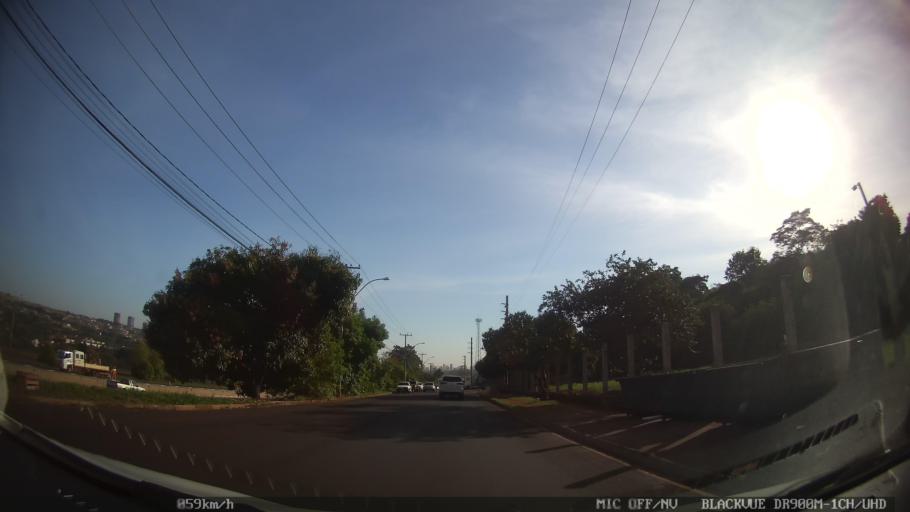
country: BR
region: Sao Paulo
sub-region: Ribeirao Preto
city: Ribeirao Preto
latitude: -21.2530
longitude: -47.8189
